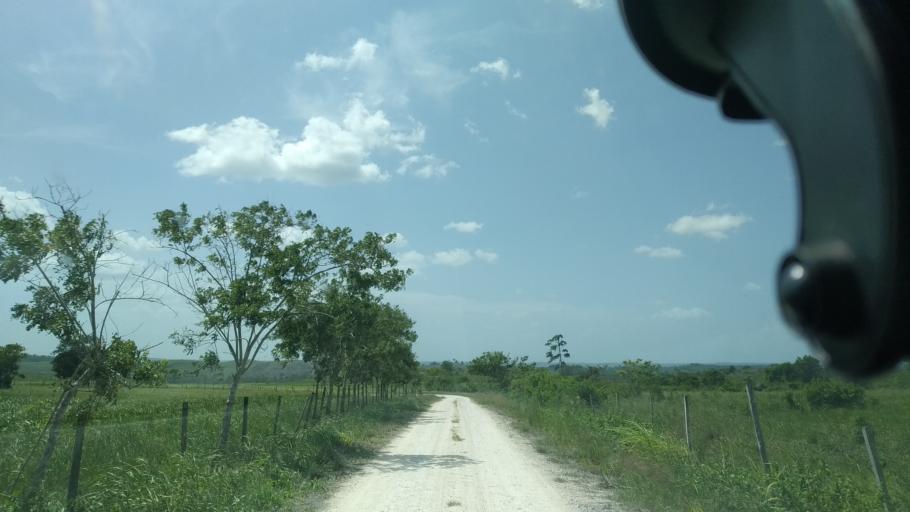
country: BZ
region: Cayo
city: San Ignacio
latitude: 17.2925
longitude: -89.0688
